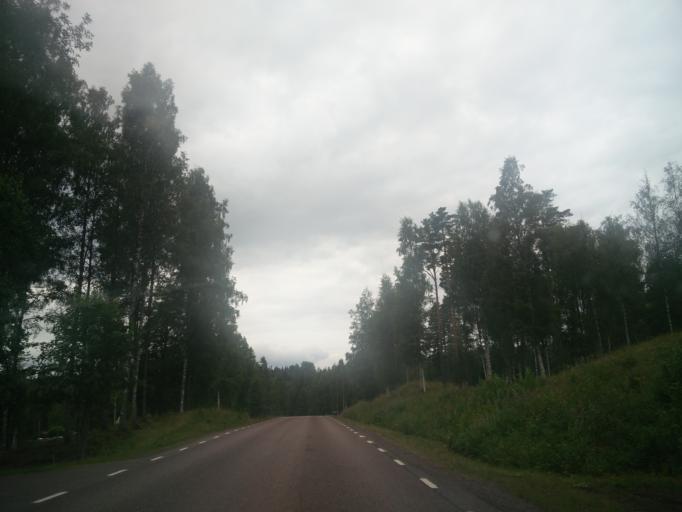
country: SE
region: Vaermland
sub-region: Arvika Kommun
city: Arvika
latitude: 59.9551
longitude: 12.7230
